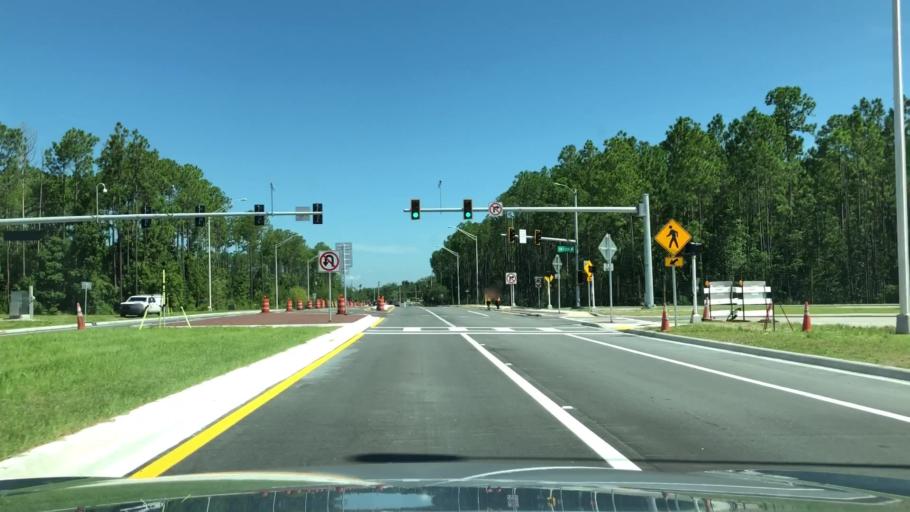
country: US
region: Florida
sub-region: Saint Johns County
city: Fruit Cove
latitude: 30.0807
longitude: -81.5320
